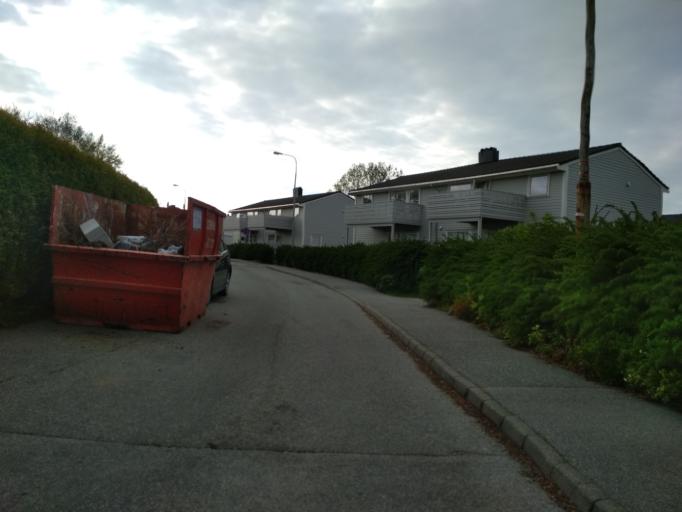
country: NO
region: Rogaland
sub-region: Stavanger
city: Stavanger
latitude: 58.9507
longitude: 5.7313
